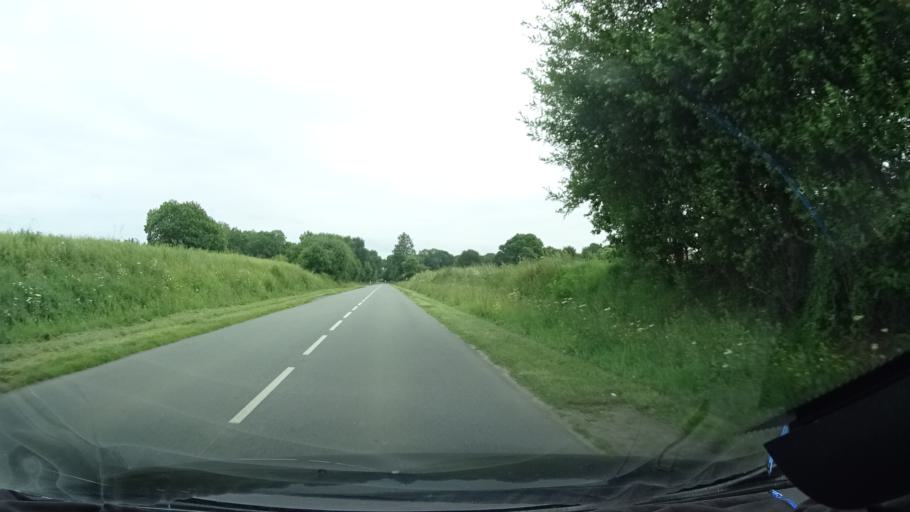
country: FR
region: Brittany
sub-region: Departement d'Ille-et-Vilaine
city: Le Minihic-sur-Rance
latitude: 48.5699
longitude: -2.0155
